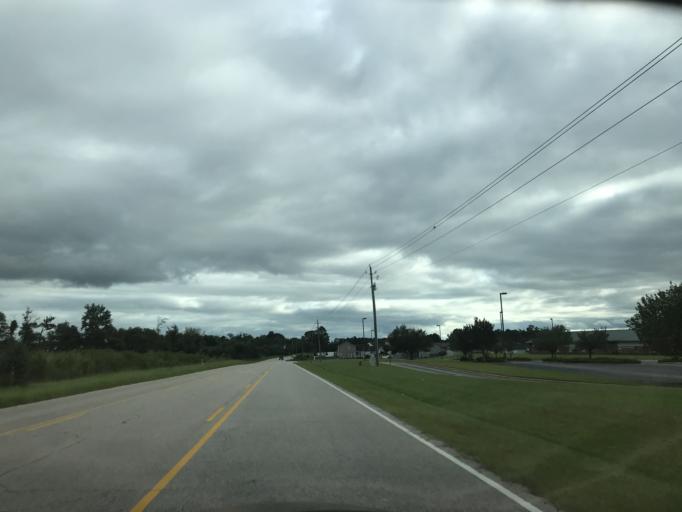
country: US
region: North Carolina
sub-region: Johnston County
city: Clayton
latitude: 35.5753
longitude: -78.5472
